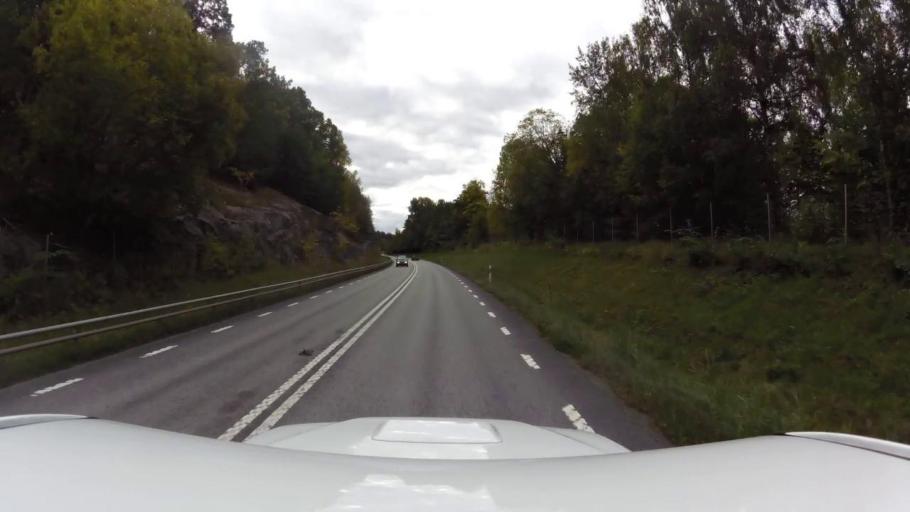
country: SE
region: OEstergoetland
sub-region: Kinda Kommun
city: Rimforsa
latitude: 58.1857
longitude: 15.6682
